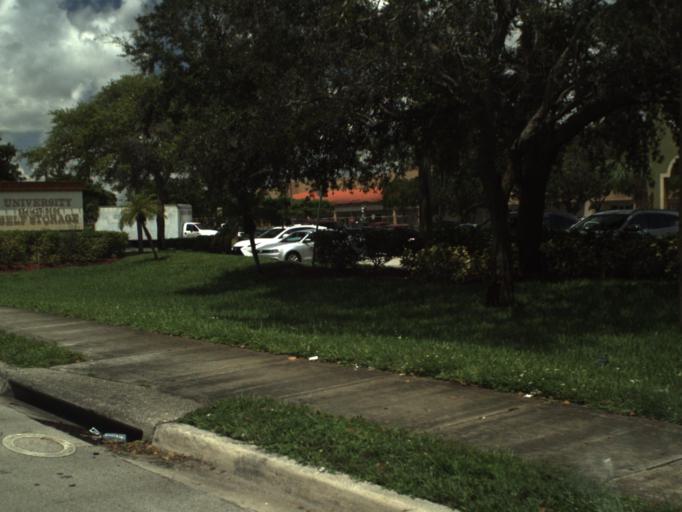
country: US
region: Florida
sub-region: Broward County
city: Pembroke Pines
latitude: 26.0092
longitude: -80.2518
